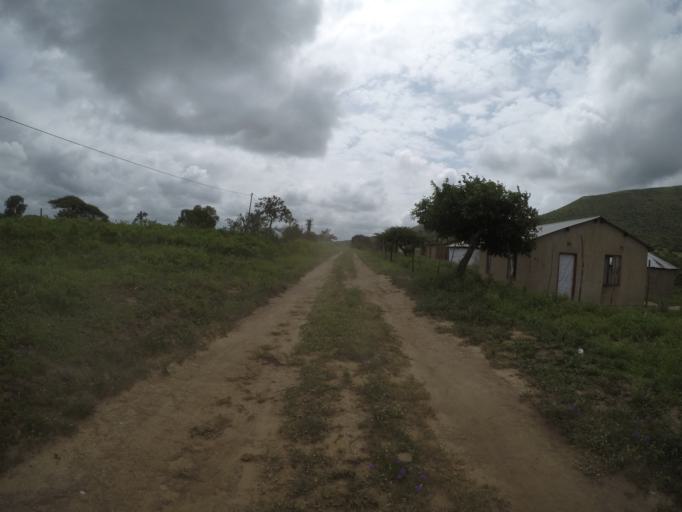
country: ZA
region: KwaZulu-Natal
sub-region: uThungulu District Municipality
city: Empangeni
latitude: -28.5805
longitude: 31.8689
